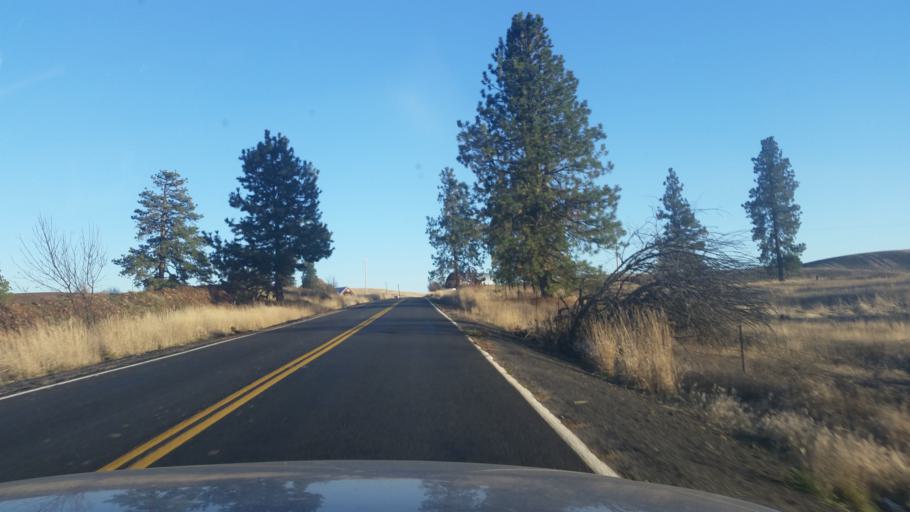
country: US
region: Washington
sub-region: Spokane County
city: Opportunity
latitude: 47.3775
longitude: -117.3083
